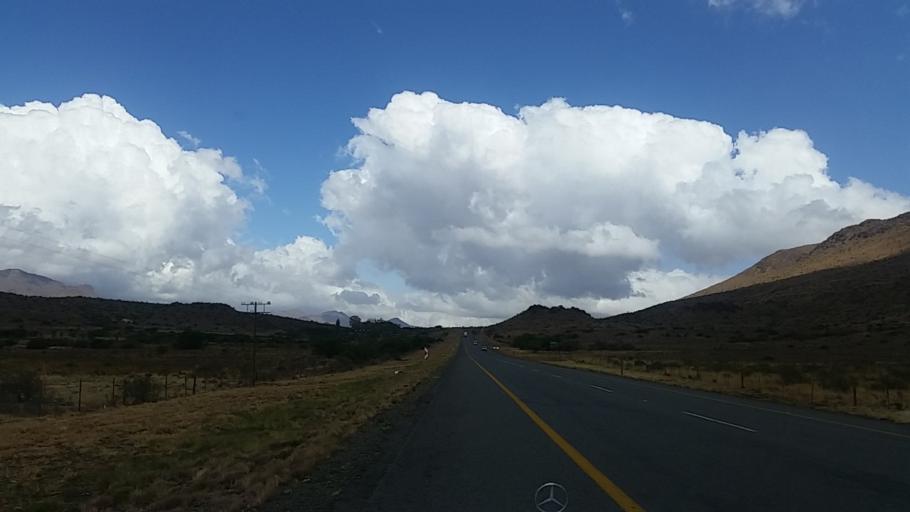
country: ZA
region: Eastern Cape
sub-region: Chris Hani District Municipality
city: Middelburg
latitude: -31.7217
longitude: 24.9533
